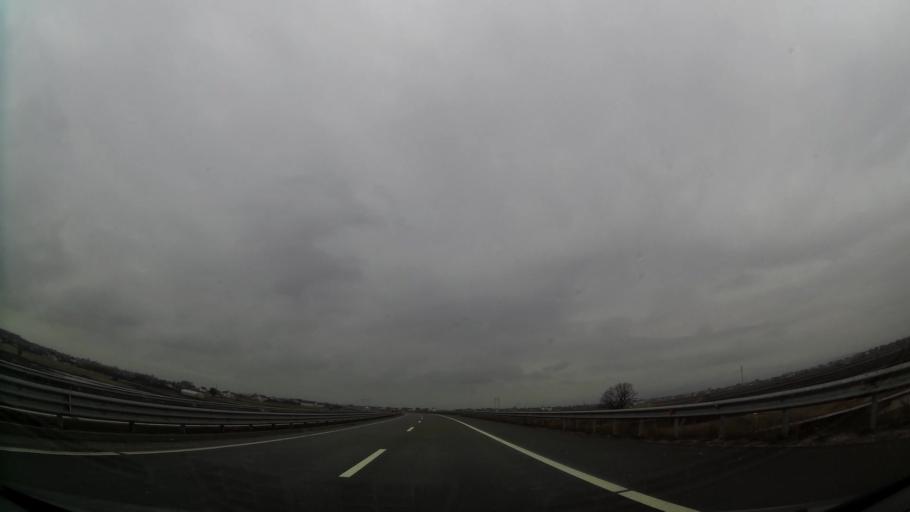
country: XK
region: Ferizaj
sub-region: Komuna e Ferizajt
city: Ferizaj
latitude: 42.4140
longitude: 21.1969
